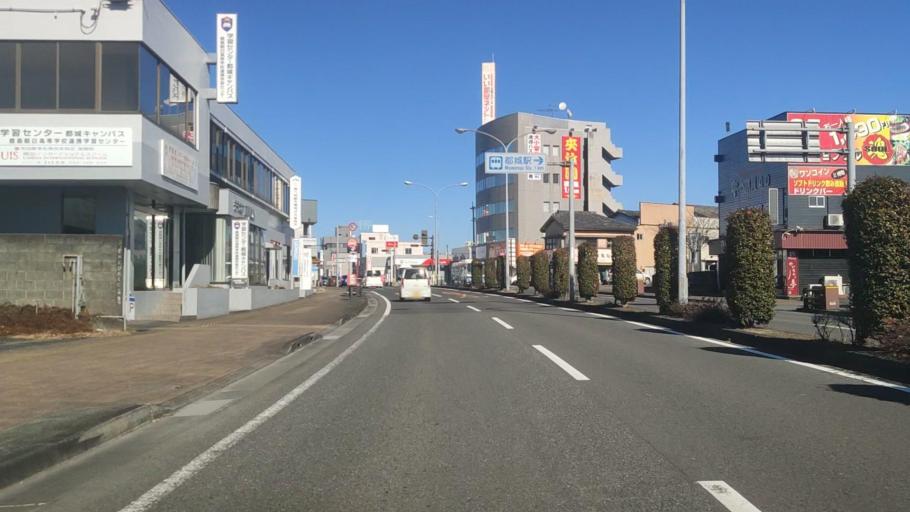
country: JP
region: Miyazaki
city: Miyakonojo
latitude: 31.7308
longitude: 131.0681
